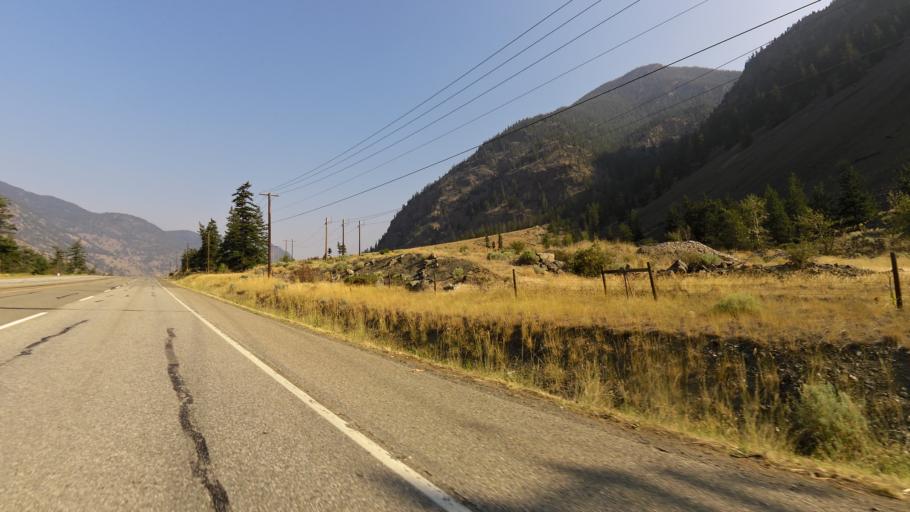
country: CA
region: British Columbia
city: Oliver
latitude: 49.2481
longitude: -120.0058
